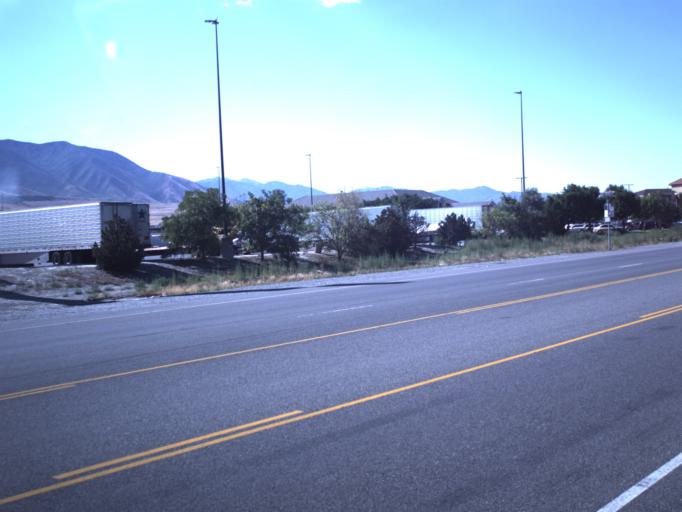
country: US
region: Utah
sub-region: Tooele County
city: Stansbury park
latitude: 40.6880
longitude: -112.2666
